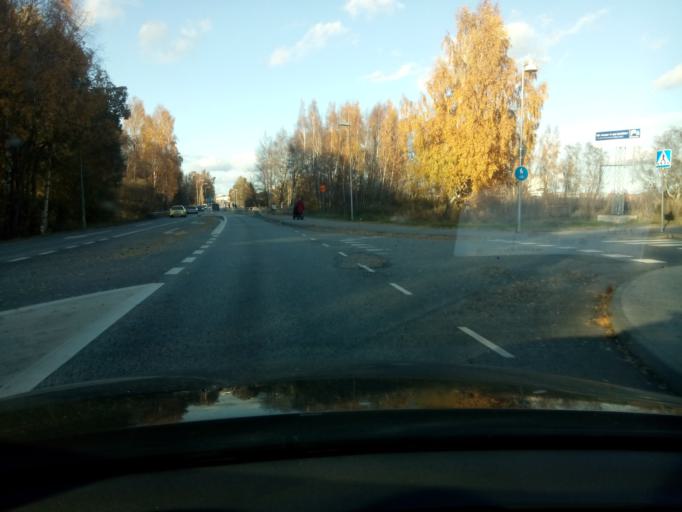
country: SE
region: Soedermanland
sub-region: Nykopings Kommun
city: Nykoping
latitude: 58.7396
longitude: 17.0062
